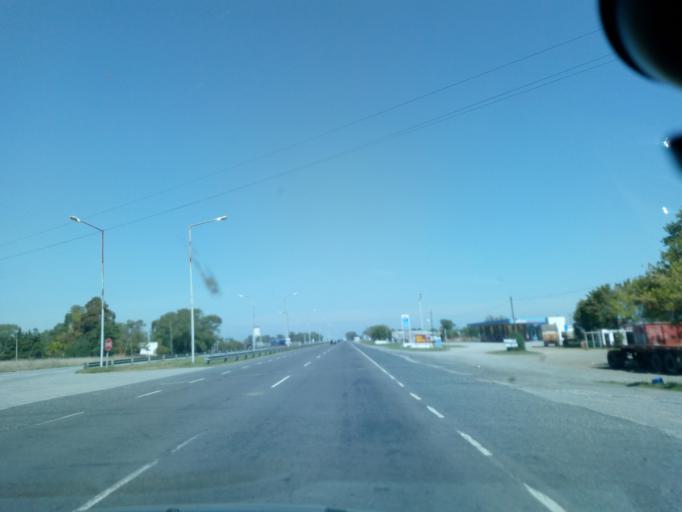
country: AR
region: Buenos Aires
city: Maipu
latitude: -36.8662
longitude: -57.8727
